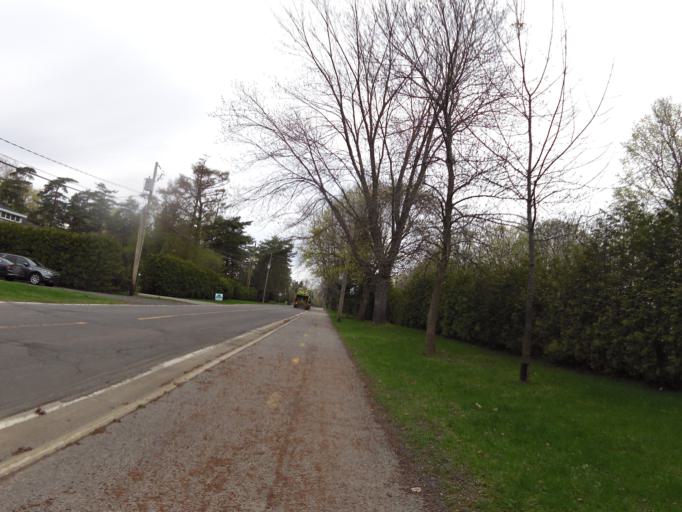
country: CA
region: Quebec
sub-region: Laurentides
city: Deux-Montagnes
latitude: 45.5276
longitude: -73.8774
